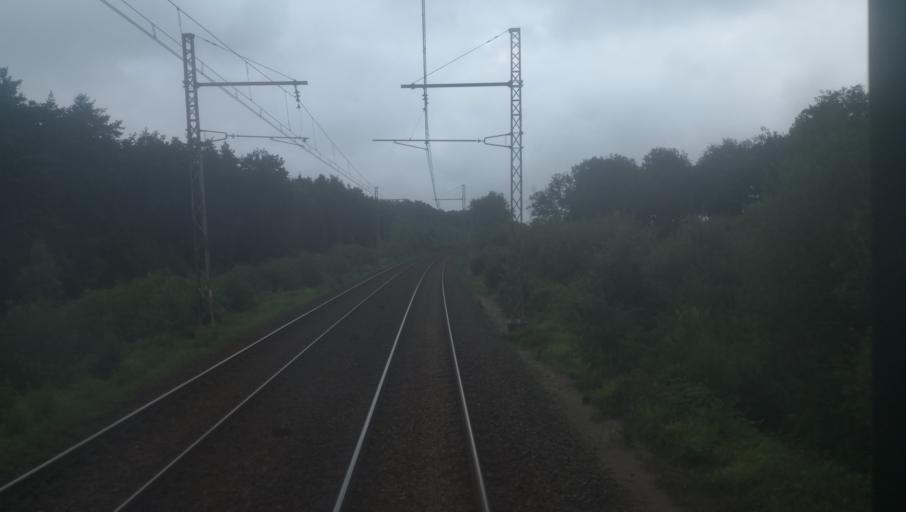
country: FR
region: Centre
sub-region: Departement de l'Indre
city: Luant
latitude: 46.7521
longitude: 1.5959
